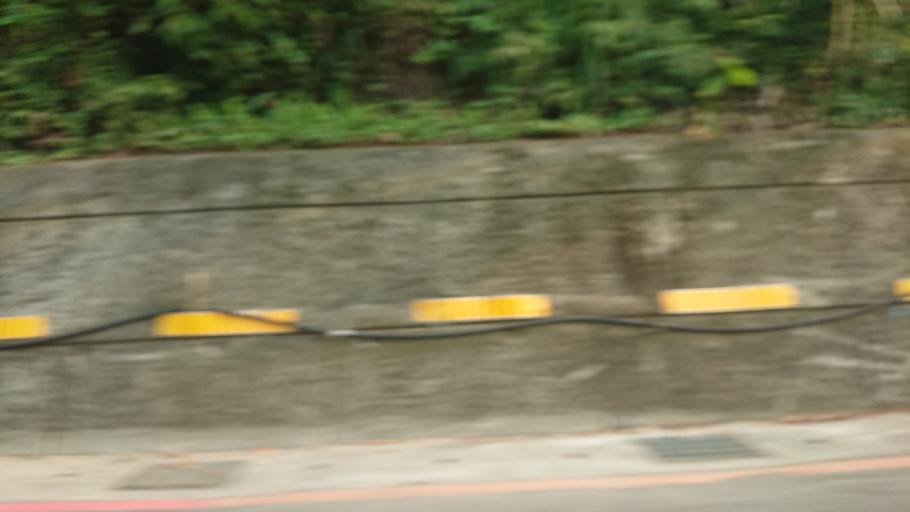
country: TW
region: Taiwan
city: Daxi
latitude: 24.8734
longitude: 121.3988
